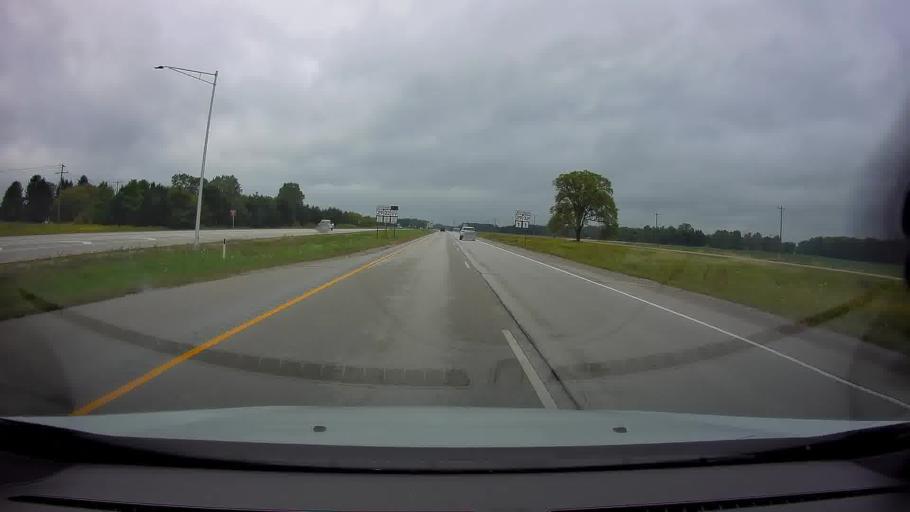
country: US
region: Wisconsin
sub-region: Brown County
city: Oneida
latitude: 44.5750
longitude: -88.1669
